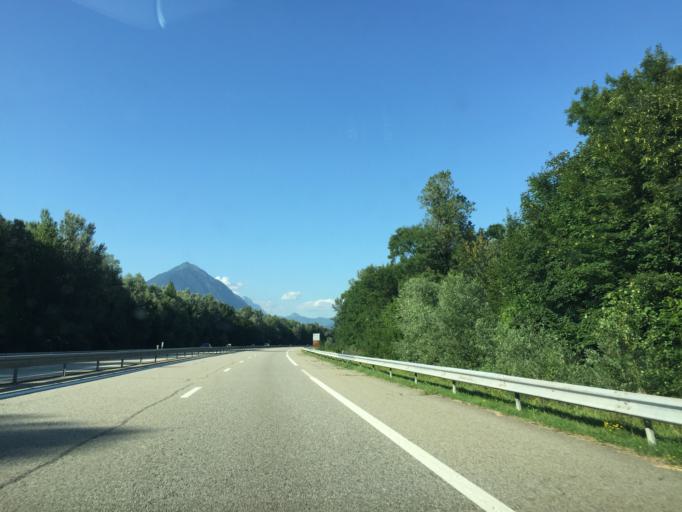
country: FR
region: Rhone-Alpes
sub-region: Departement de la Savoie
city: Gresy-sur-Isere
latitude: 45.6027
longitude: 6.2817
